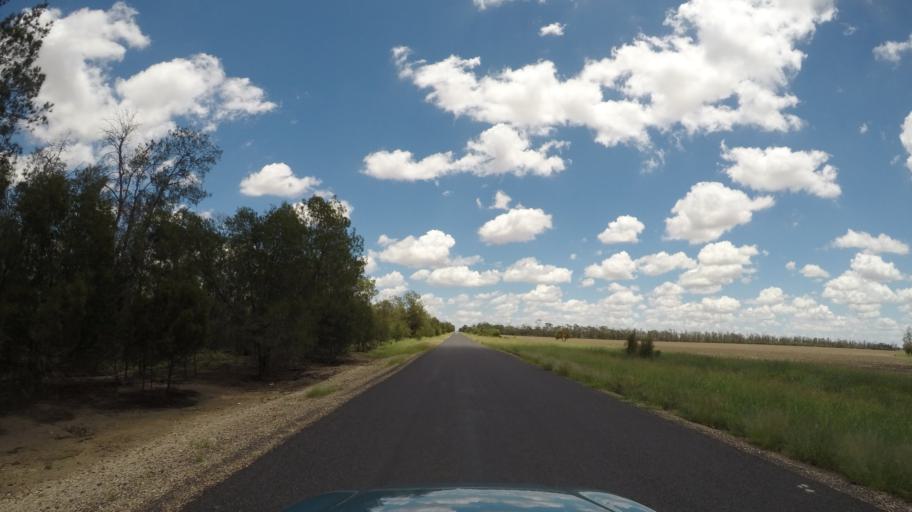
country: AU
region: Queensland
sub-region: Goondiwindi
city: Goondiwindi
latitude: -28.1699
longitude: 150.2098
